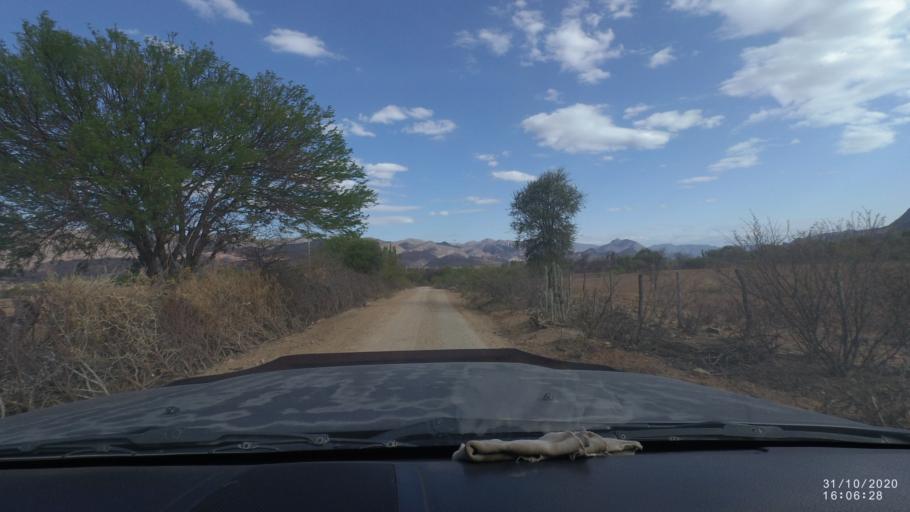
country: BO
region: Chuquisaca
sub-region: Provincia Zudanez
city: Mojocoya
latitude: -18.3734
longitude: -64.6469
